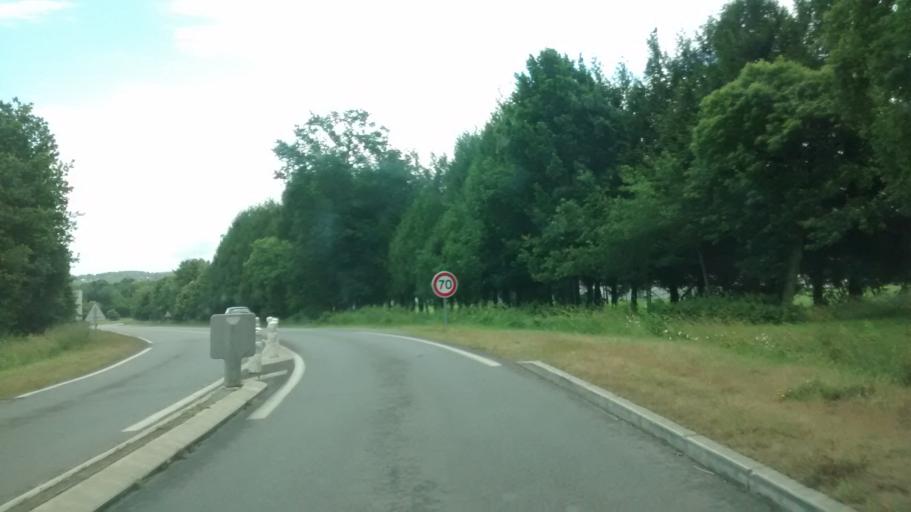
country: FR
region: Brittany
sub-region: Departement du Morbihan
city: La Gacilly
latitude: 47.7747
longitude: -2.1298
